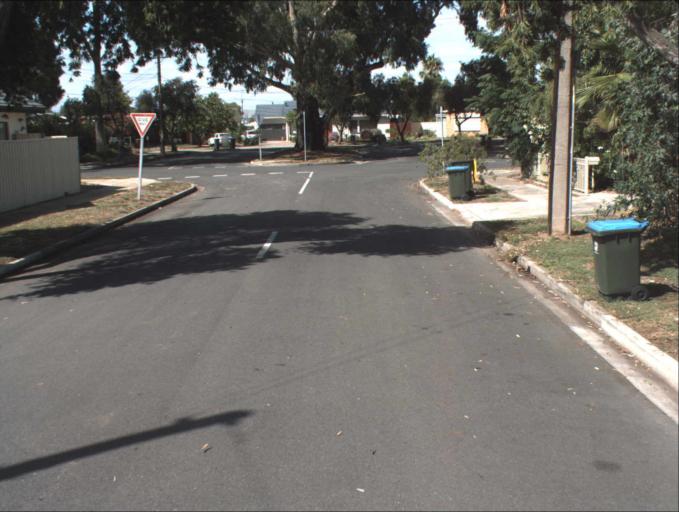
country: AU
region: South Australia
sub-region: Prospect
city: Prospect
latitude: -34.8766
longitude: 138.5791
